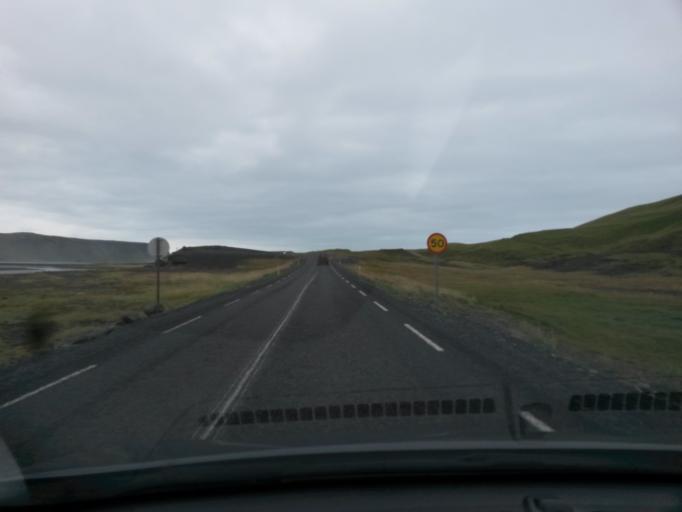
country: IS
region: South
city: Vestmannaeyjar
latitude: 63.4102
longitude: -19.1247
